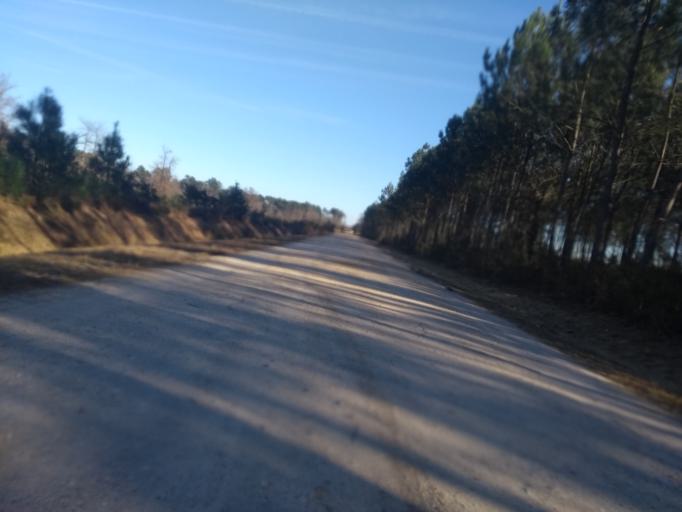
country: FR
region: Aquitaine
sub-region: Departement de la Gironde
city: Le Barp
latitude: 44.6151
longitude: -0.7893
